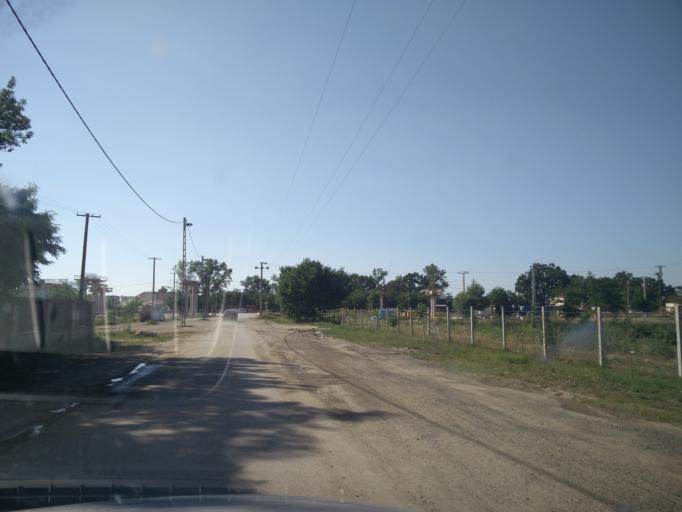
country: HU
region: Csongrad
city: Hodmezovasarhely
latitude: 46.3861
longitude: 20.2719
